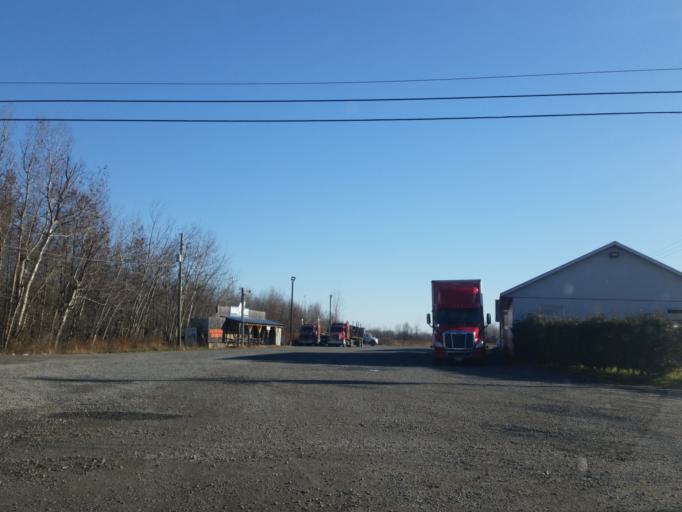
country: CA
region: Quebec
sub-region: Mauricie
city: Yamachiche
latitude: 46.2622
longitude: -72.8753
